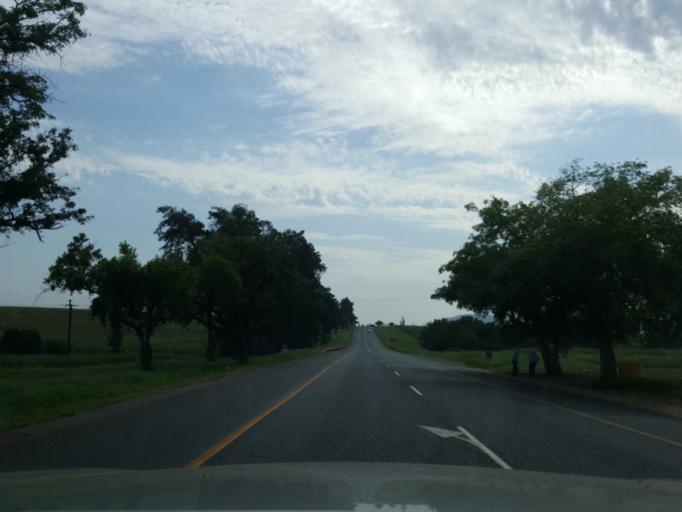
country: SZ
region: Hhohho
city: Ntfonjeni
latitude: -25.5119
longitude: 31.4658
